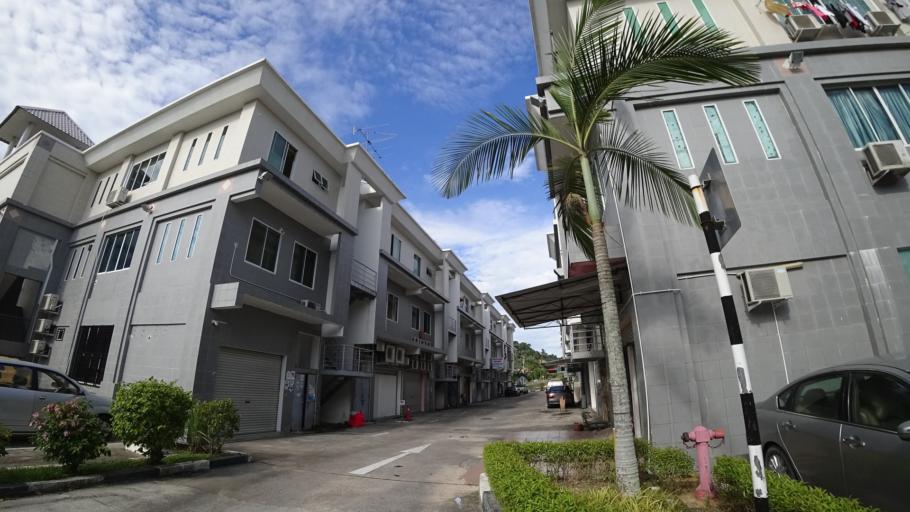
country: BN
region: Brunei and Muara
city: Bandar Seri Begawan
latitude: 4.8904
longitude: 114.8563
